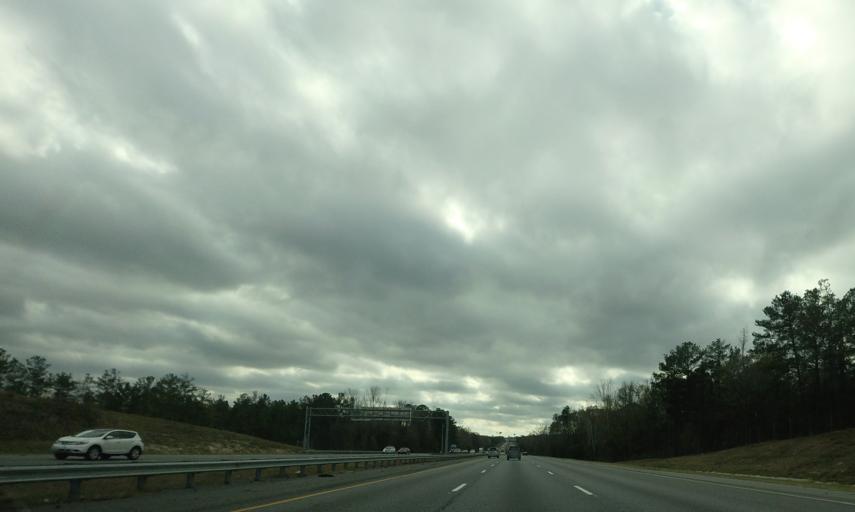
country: US
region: Georgia
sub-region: Peach County
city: Byron
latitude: 32.7023
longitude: -83.7349
